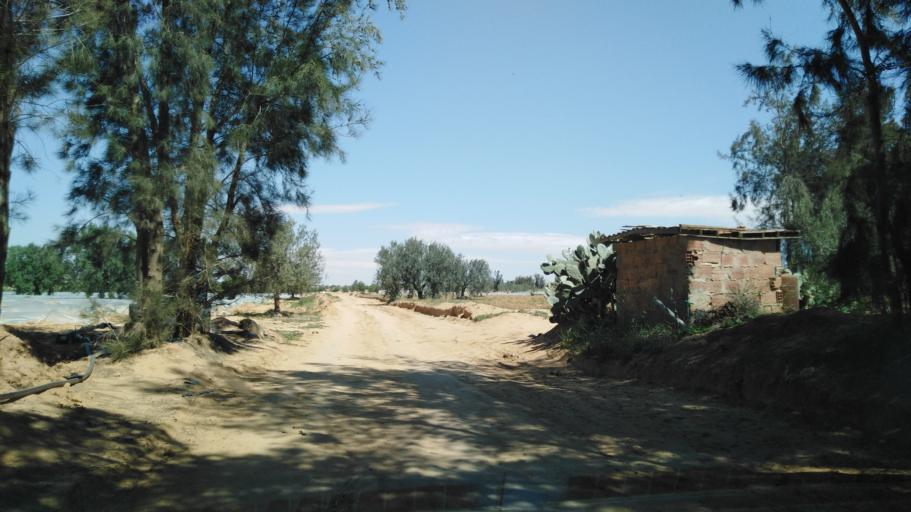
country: TN
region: Safaqis
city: Sfax
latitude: 34.7665
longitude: 10.5279
